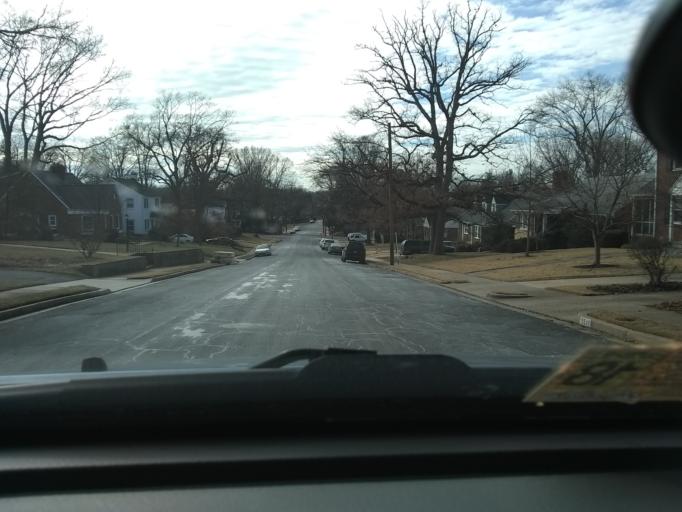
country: US
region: Virginia
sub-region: Fairfax County
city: Seven Corners
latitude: 38.8889
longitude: -77.1347
